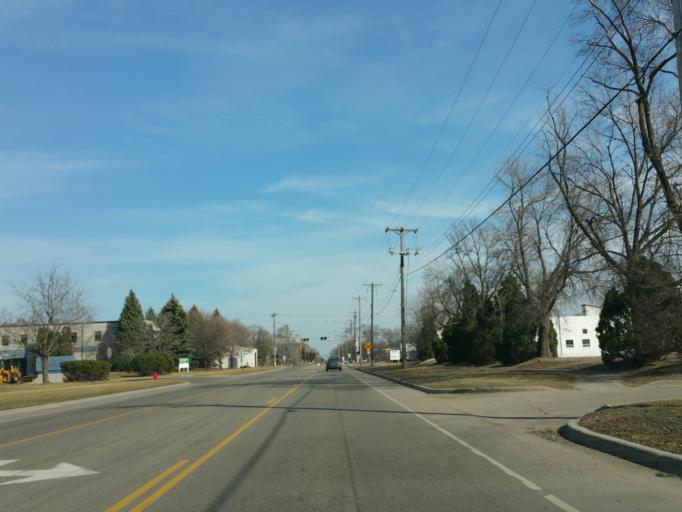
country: US
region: Minnesota
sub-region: Hennepin County
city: Bloomington
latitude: 44.8479
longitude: -93.2856
